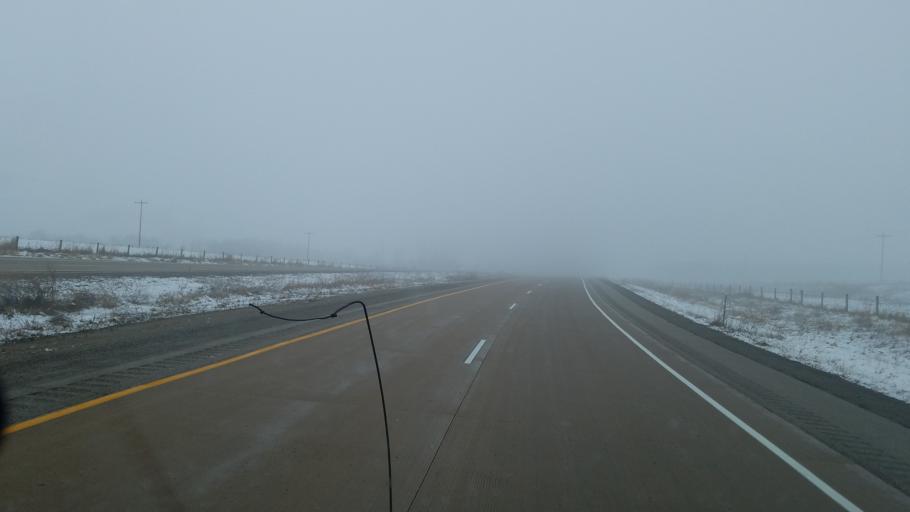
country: US
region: Wisconsin
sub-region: Winnebago County
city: Winneconne
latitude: 44.1367
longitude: -88.6641
